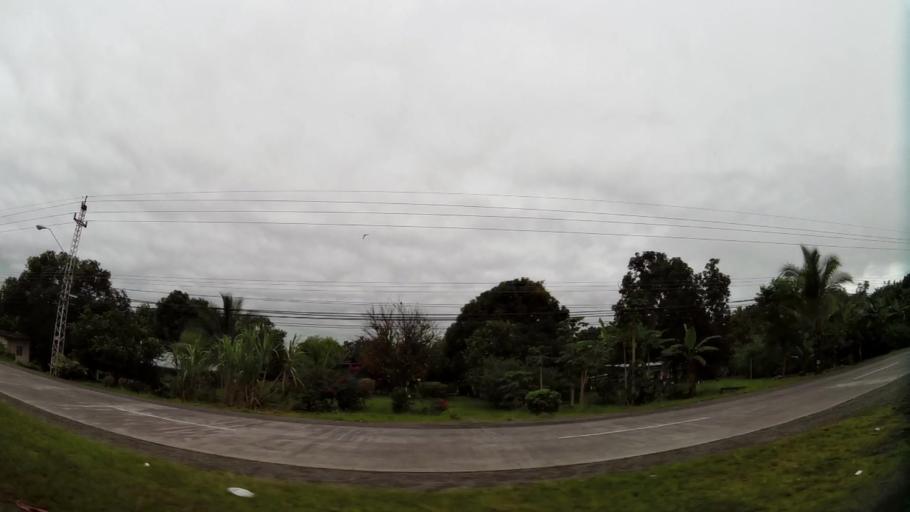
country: PA
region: Chiriqui
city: Boqueron
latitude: 8.4924
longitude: -82.5808
